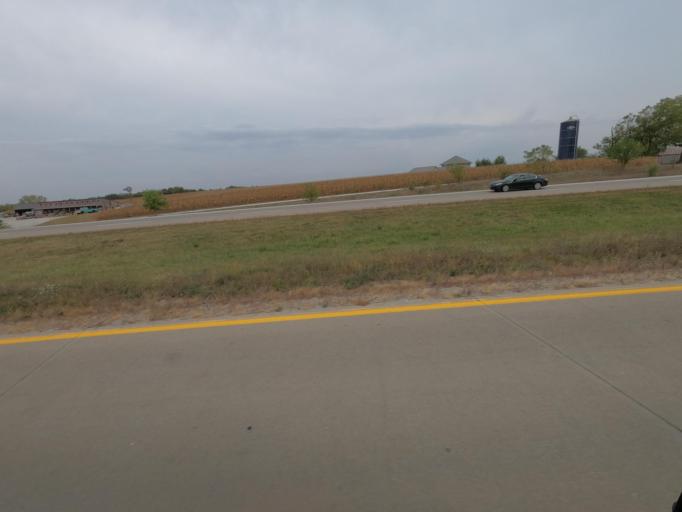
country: US
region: Iowa
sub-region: Marion County
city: Pella
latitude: 41.3857
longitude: -92.8250
